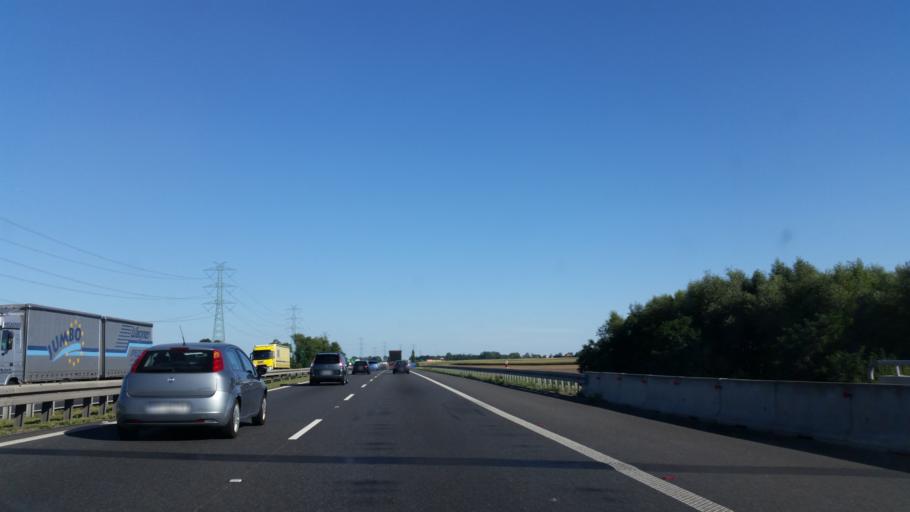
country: PL
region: Lower Silesian Voivodeship
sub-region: Powiat olawski
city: Wierzbno
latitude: 50.9037
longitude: 17.1649
